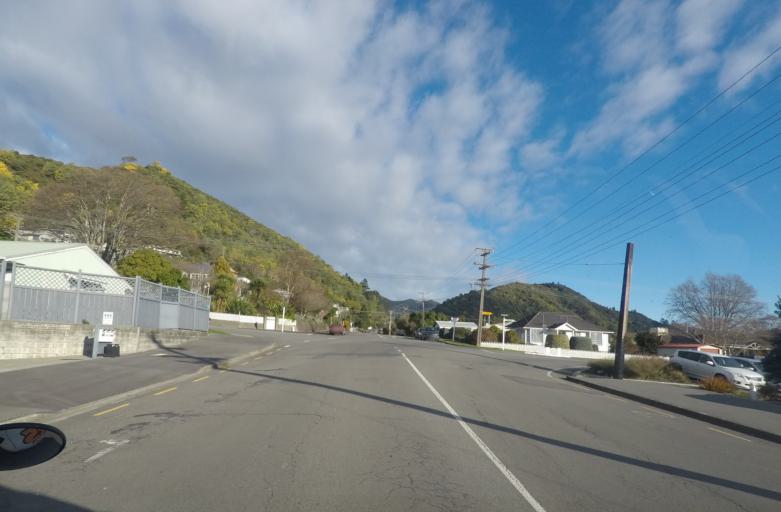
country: NZ
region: Marlborough
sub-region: Marlborough District
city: Picton
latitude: -41.2926
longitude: 174.0078
